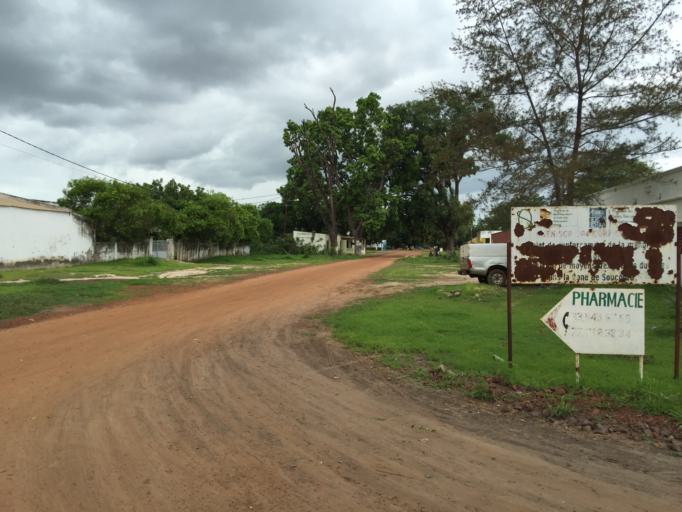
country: SN
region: Fatick
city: Sokone
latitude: 13.7863
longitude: -16.4738
